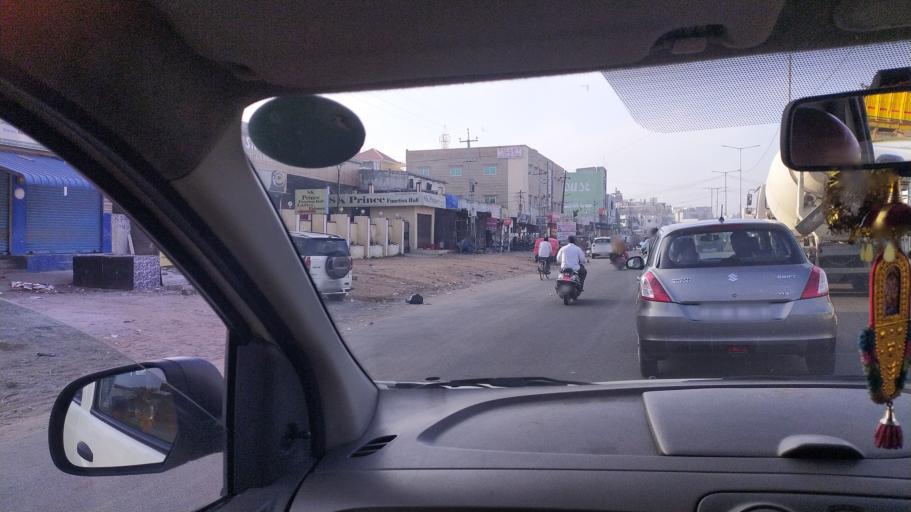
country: IN
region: Telangana
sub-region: Rangareddi
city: Balapur
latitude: 17.3192
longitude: 78.4670
